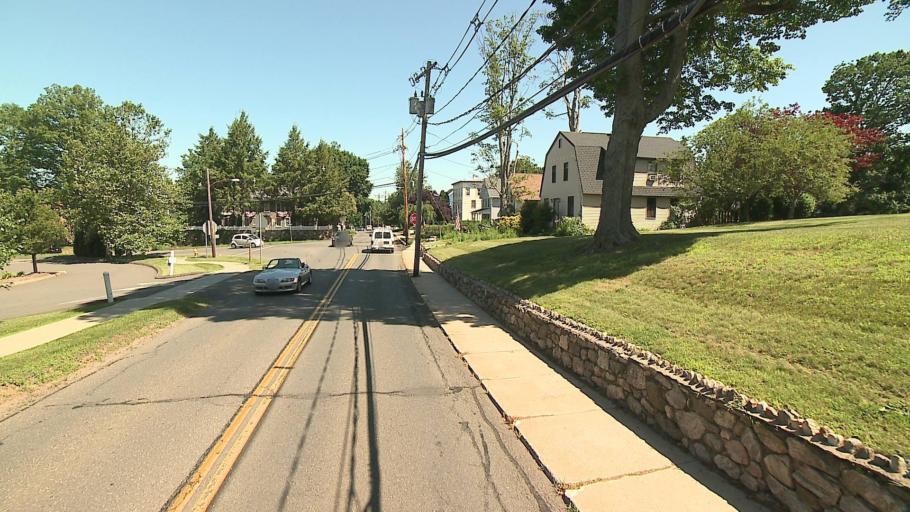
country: US
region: Connecticut
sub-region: Fairfield County
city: Ridgefield
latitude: 41.2820
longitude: -73.5040
